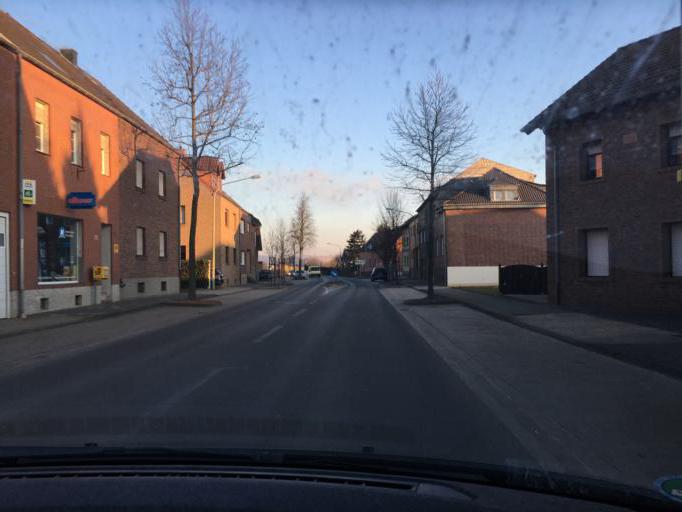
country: DE
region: North Rhine-Westphalia
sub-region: Regierungsbezirk Koln
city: Niederzier
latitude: 50.8687
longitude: 6.4748
